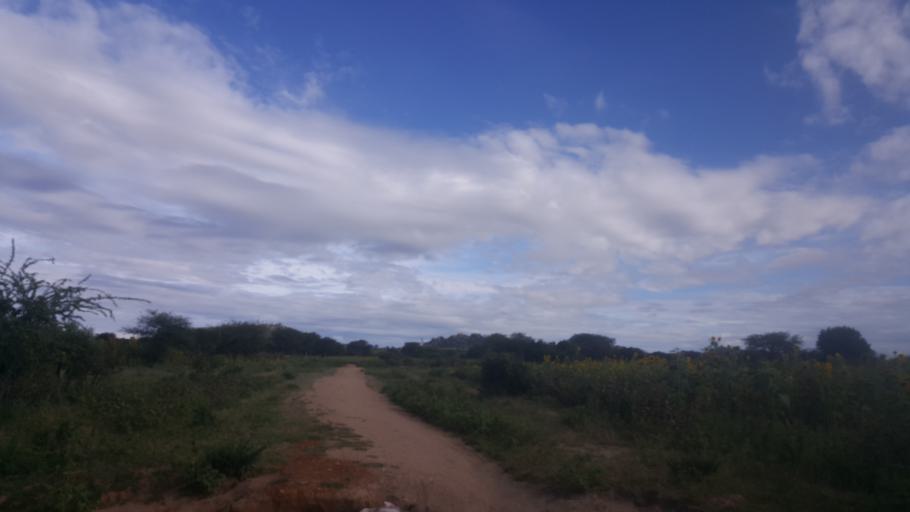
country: TZ
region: Dodoma
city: Dodoma
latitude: -6.0875
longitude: 35.5234
